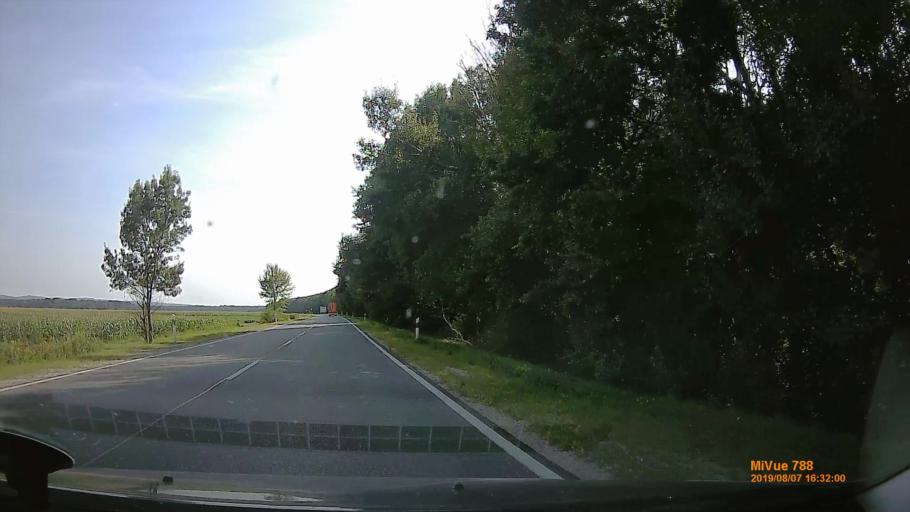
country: HU
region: Zala
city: Lenti
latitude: 46.6518
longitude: 16.4948
